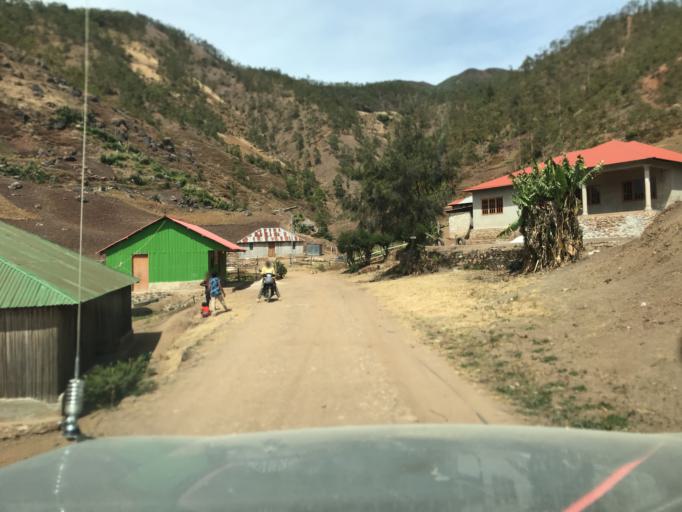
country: TL
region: Ainaro
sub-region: Ainaro
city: Ainaro
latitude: -8.8920
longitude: 125.5177
